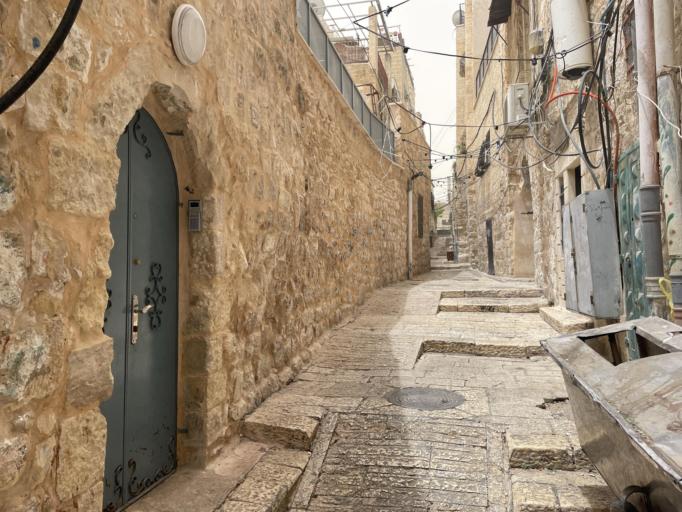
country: PS
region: West Bank
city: East Jerusalem
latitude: 31.7813
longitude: 35.2343
